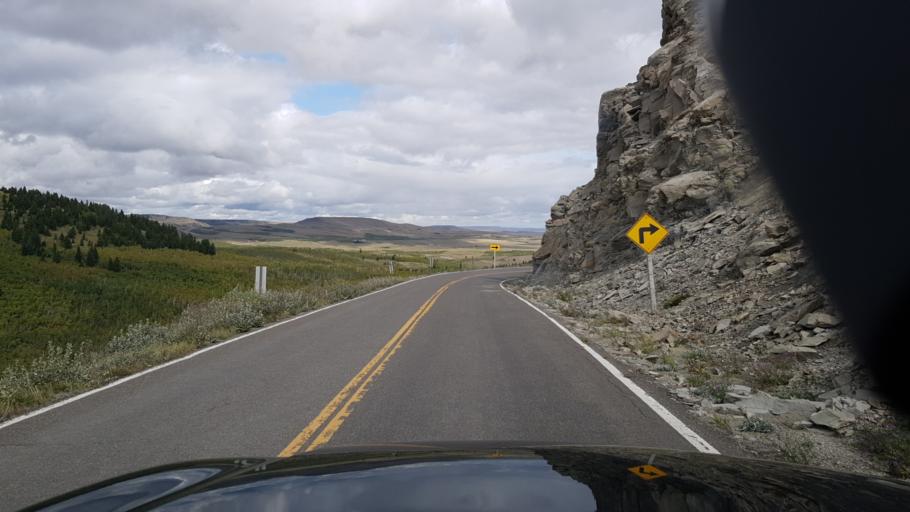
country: US
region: Montana
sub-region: Glacier County
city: South Browning
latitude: 48.5454
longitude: -113.2923
